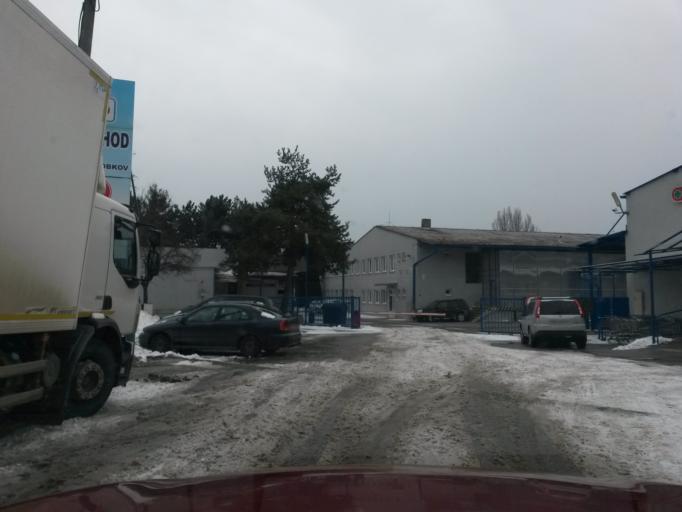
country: SK
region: Kosicky
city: Kosice
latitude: 48.7090
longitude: 21.2710
